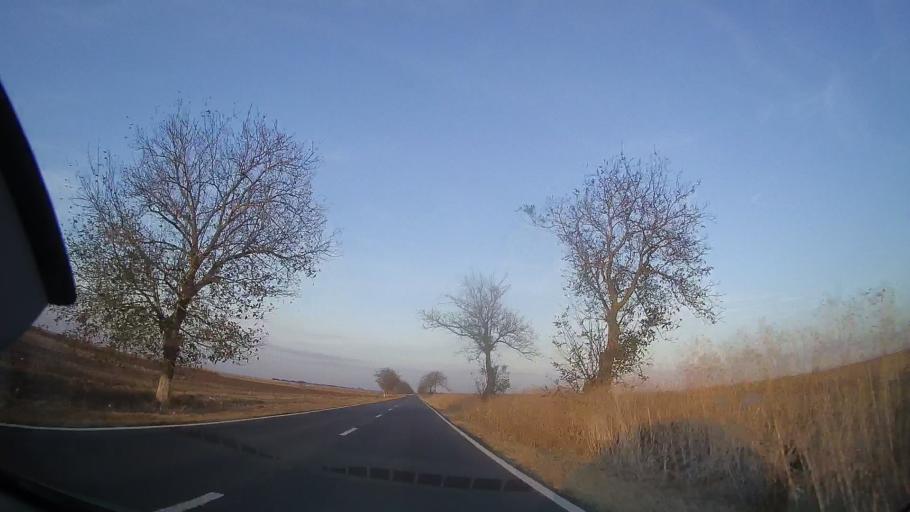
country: RO
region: Constanta
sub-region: Comuna Topraisar
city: Topraisar
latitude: 43.9922
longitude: 28.4262
